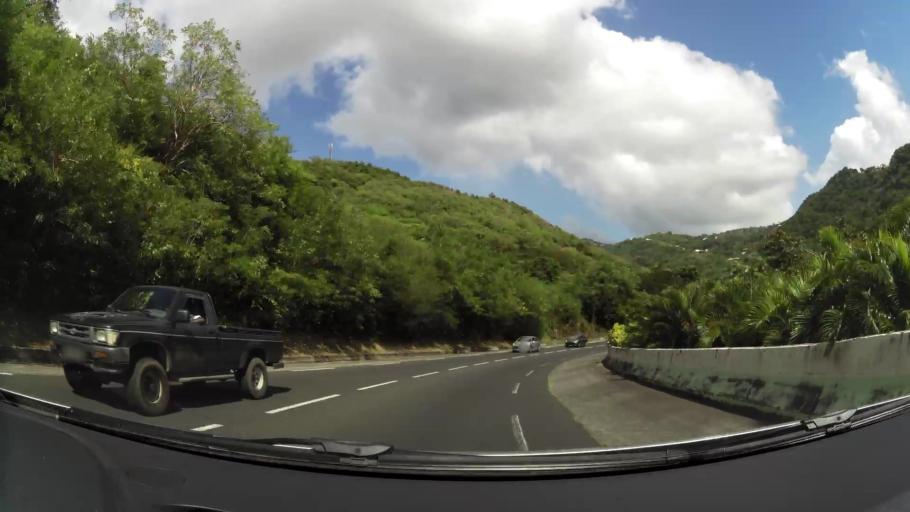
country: MQ
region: Martinique
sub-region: Martinique
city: Fort-de-France
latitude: 14.6370
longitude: -61.1318
